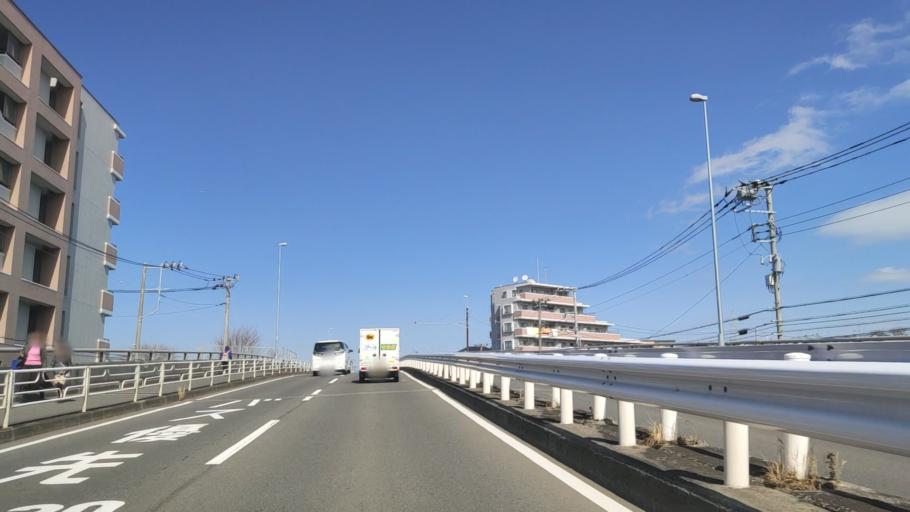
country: JP
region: Kanagawa
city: Yokohama
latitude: 35.4925
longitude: 139.6073
